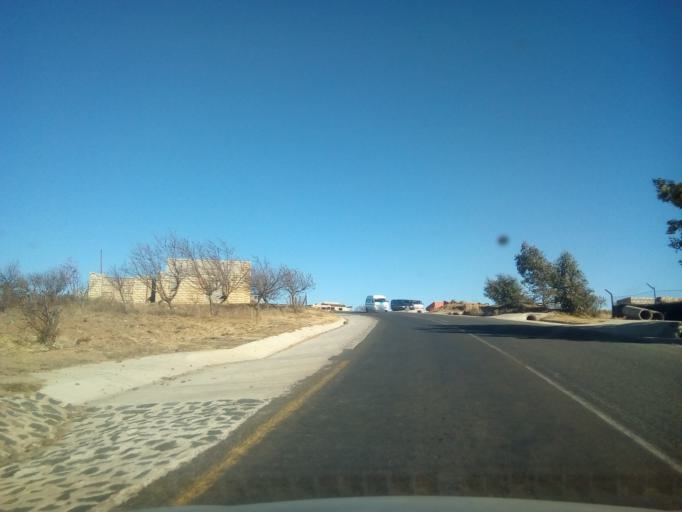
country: LS
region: Maseru
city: Maseru
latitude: -29.2930
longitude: 27.6202
